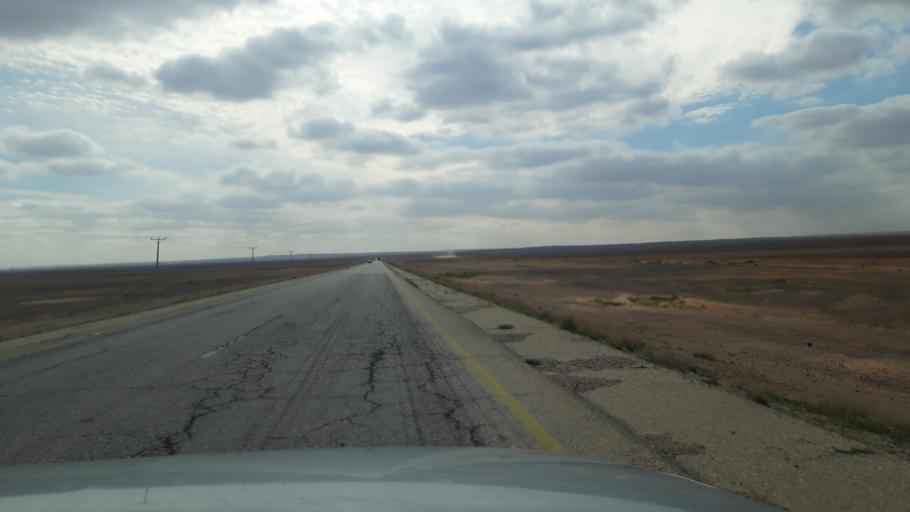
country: JO
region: Amman
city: Al Azraq ash Shamali
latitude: 31.8364
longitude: 36.6346
